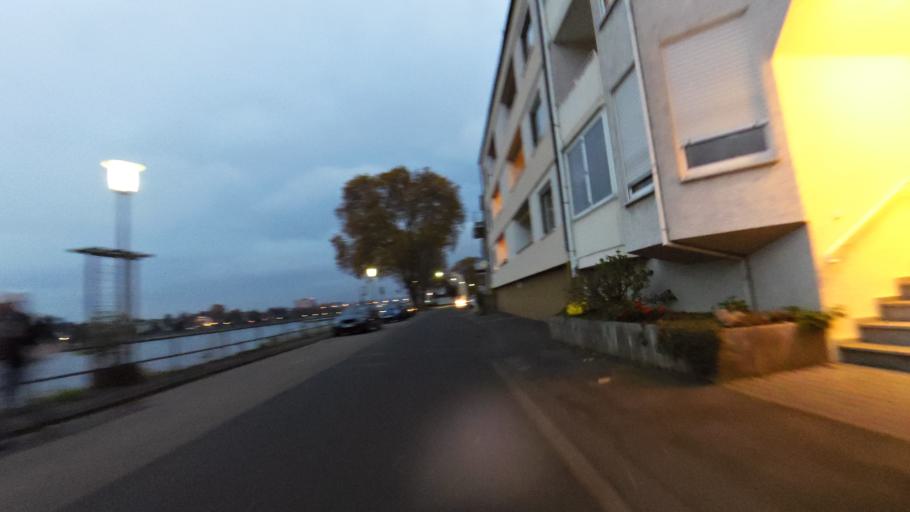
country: DE
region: Rheinland-Pfalz
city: Koblenz
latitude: 50.3426
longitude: 7.5999
